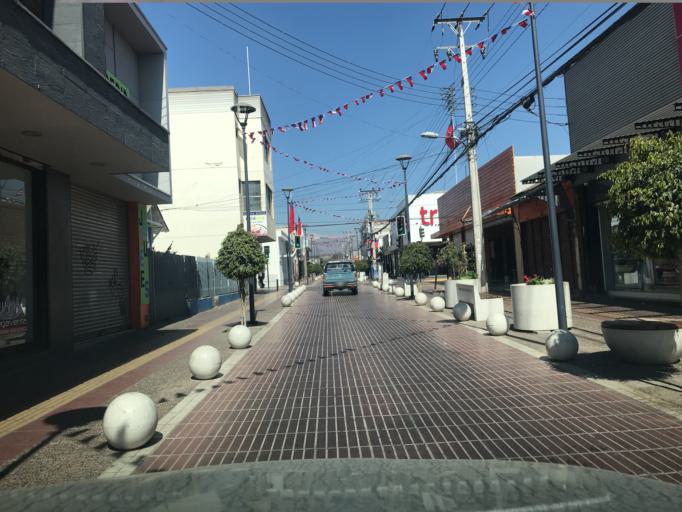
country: CL
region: Atacama
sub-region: Provincia de Huasco
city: Vallenar
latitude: -28.5776
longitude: -70.7573
